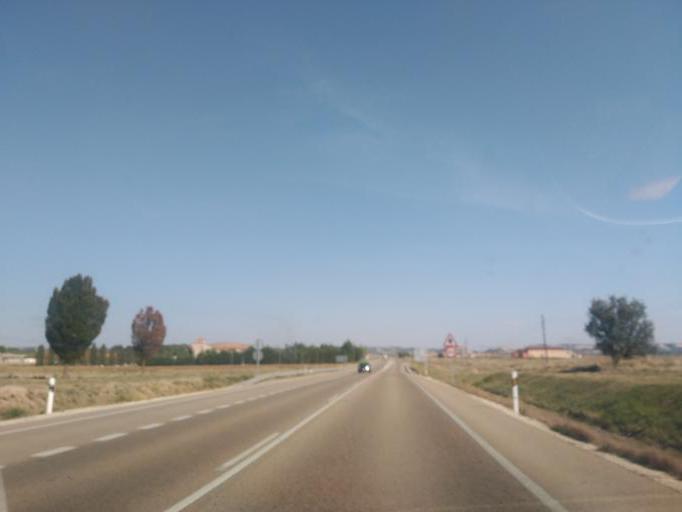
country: ES
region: Castille and Leon
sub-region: Provincia de Valladolid
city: Manzanillo
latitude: 41.6120
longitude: -4.1719
